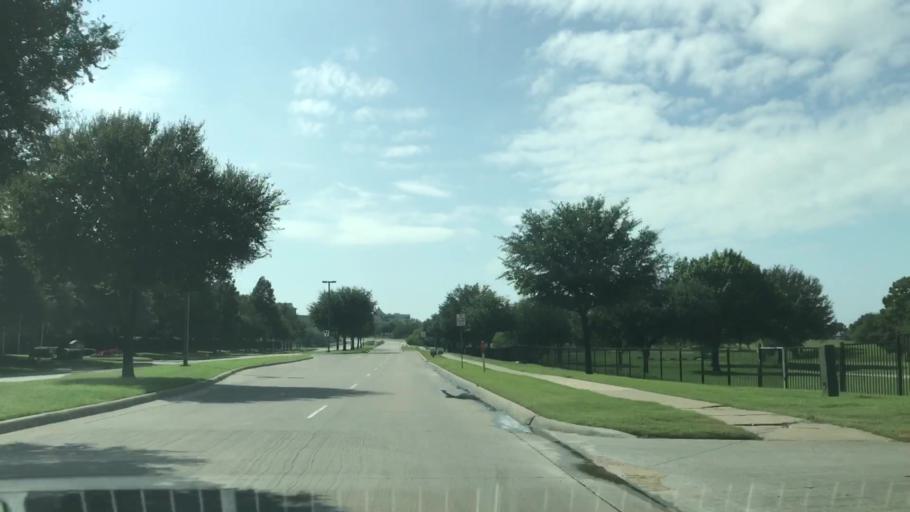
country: US
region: Texas
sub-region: Dallas County
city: Coppell
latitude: 32.9035
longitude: -96.9665
